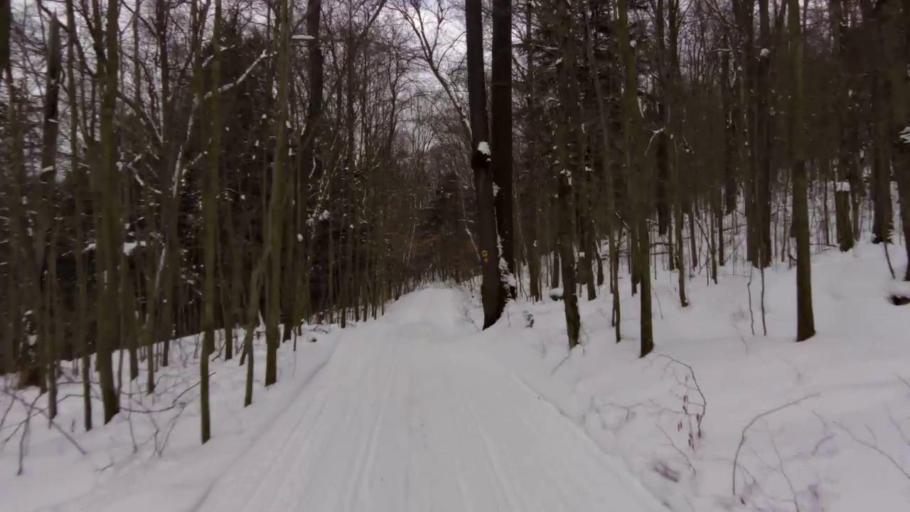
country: US
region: Pennsylvania
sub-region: McKean County
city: Bradford
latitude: 42.0163
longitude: -78.7241
